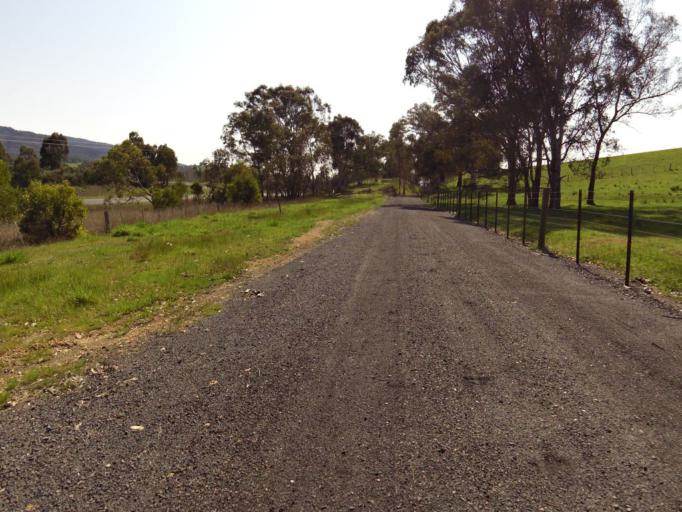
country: AU
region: Victoria
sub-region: Murrindindi
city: Alexandra
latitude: -37.1330
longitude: 145.5931
